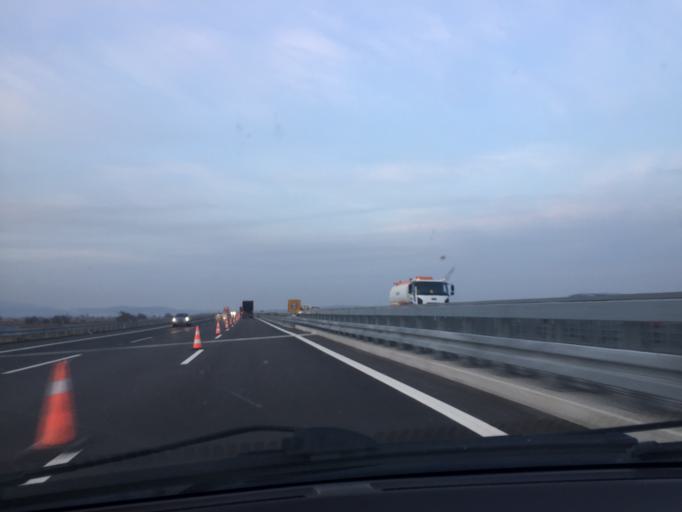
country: TR
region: Manisa
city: Halitpasa
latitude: 38.7241
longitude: 27.6529
